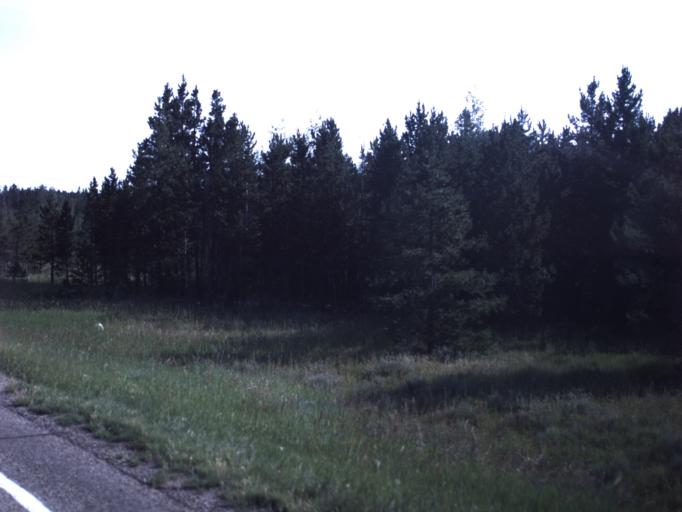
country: US
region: Utah
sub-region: Daggett County
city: Manila
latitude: 40.8071
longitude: -109.4676
